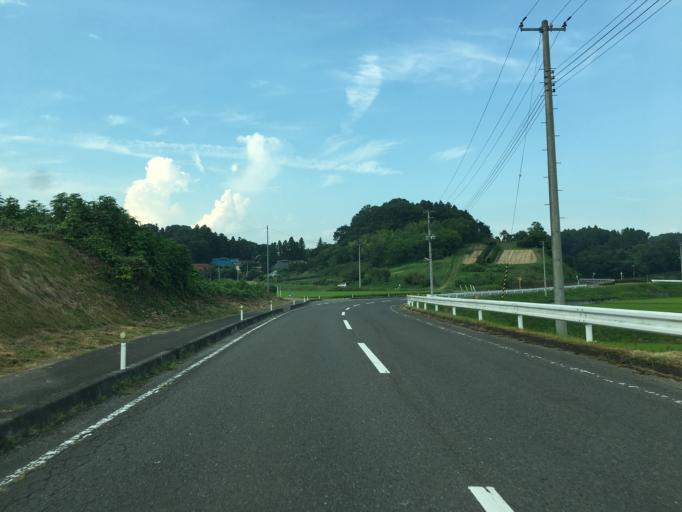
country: JP
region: Fukushima
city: Motomiya
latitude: 37.5153
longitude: 140.4421
